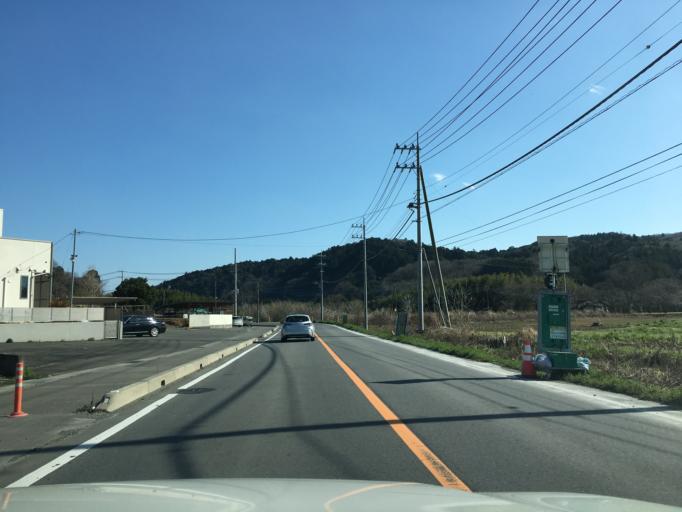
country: JP
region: Ibaraki
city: Omiya
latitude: 36.5558
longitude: 140.3192
